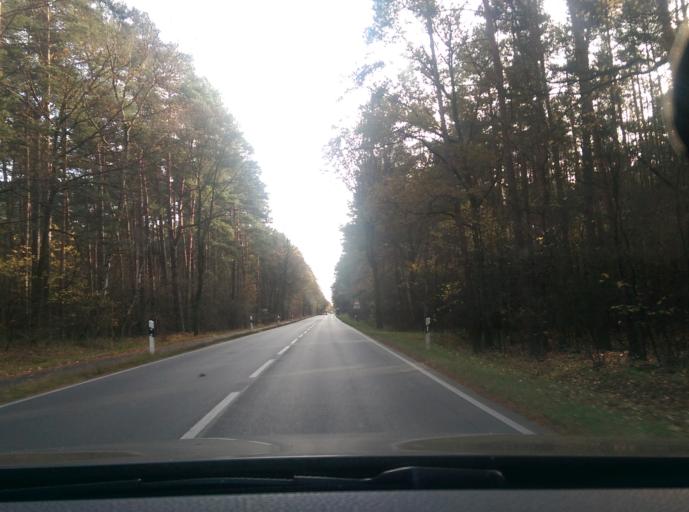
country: DE
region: Lower Saxony
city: Hambuhren
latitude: 52.6664
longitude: 9.9759
